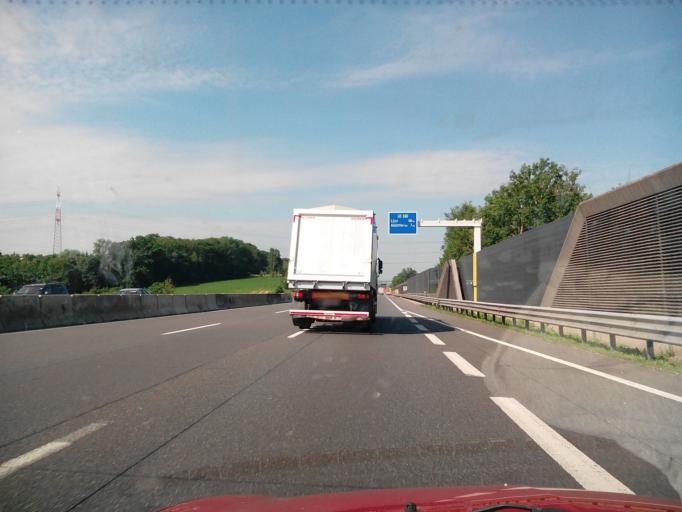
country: AT
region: Lower Austria
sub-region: Politischer Bezirk Melk
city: Ybbs an der Donau
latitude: 48.1517
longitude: 15.0958
